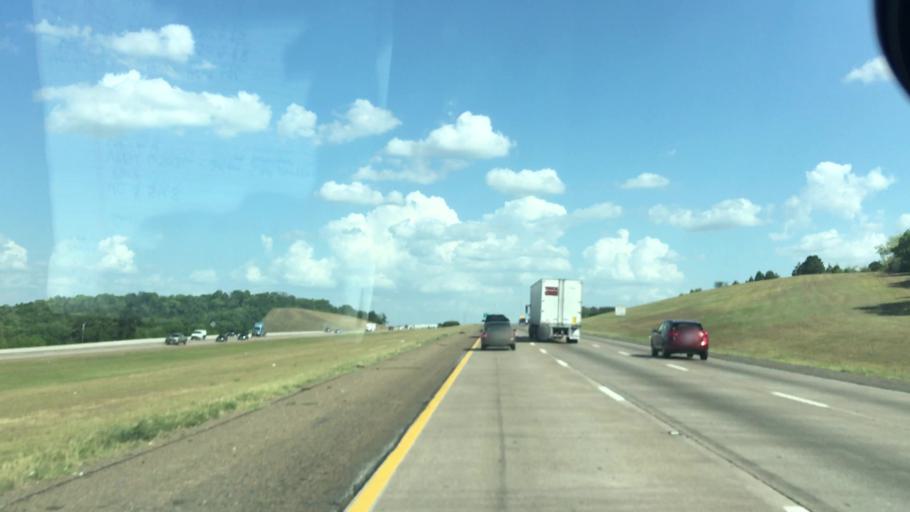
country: US
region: Texas
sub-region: Dallas County
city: Hutchins
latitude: 32.6717
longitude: -96.7359
